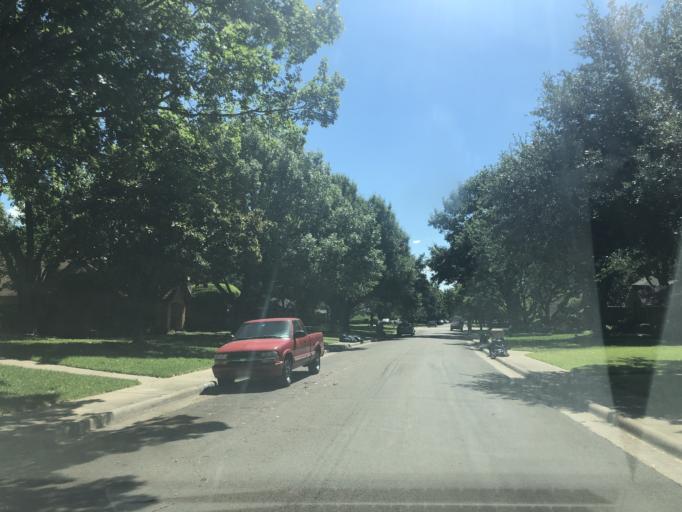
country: US
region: Texas
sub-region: Dallas County
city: Duncanville
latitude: 32.6439
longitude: -96.9318
